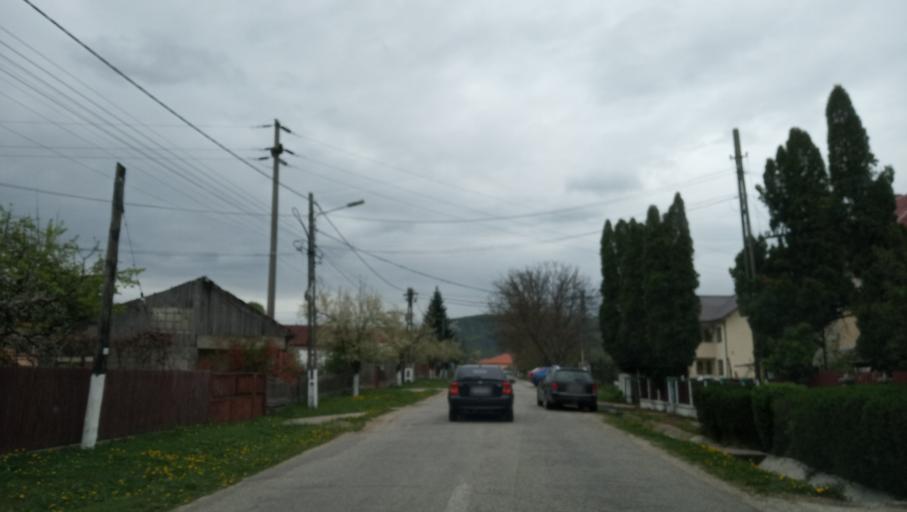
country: RO
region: Valcea
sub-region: Comuna Daesti
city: Daesti
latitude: 45.1789
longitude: 24.3794
